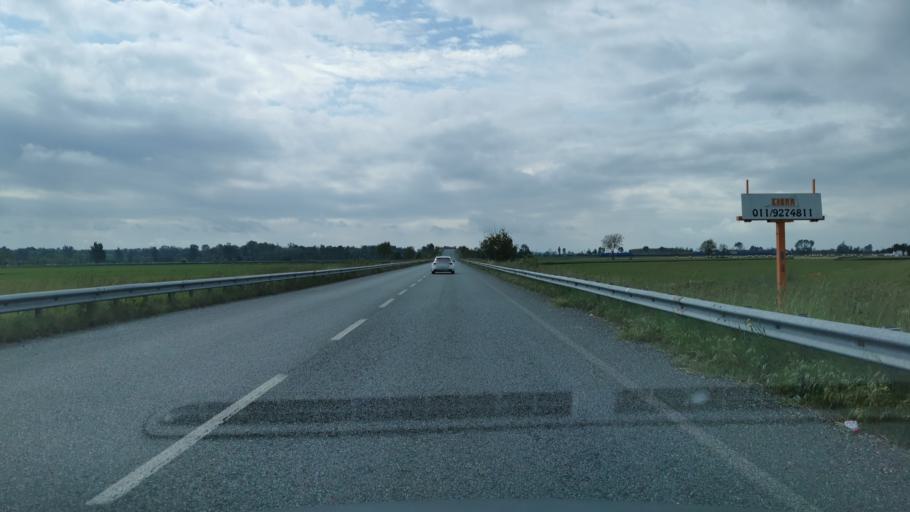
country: IT
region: Piedmont
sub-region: Provincia di Cuneo
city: Racconigi
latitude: 44.7992
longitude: 7.6940
